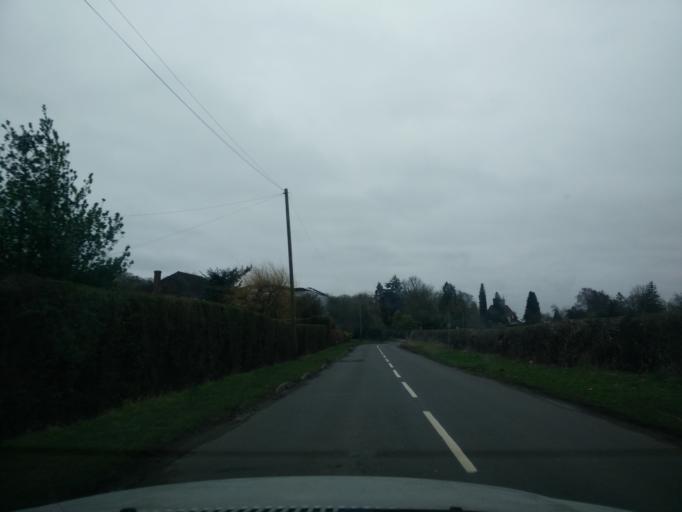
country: GB
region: England
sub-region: Buckinghamshire
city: Little Chalfont
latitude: 51.6592
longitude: -0.5732
